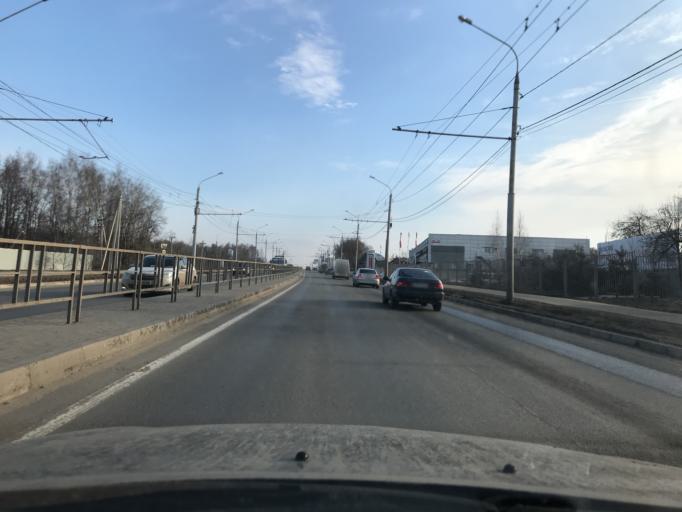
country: RU
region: Kaluga
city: Kaluga
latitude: 54.4978
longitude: 36.2287
